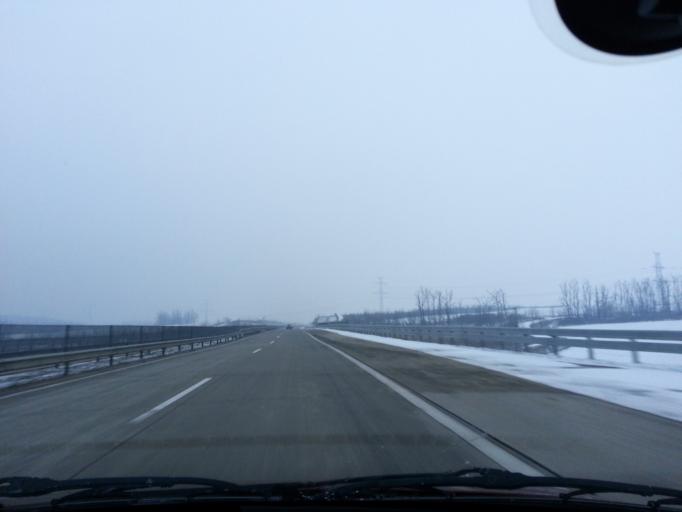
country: HU
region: Pest
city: Kerepes
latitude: 47.5551
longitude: 19.3158
